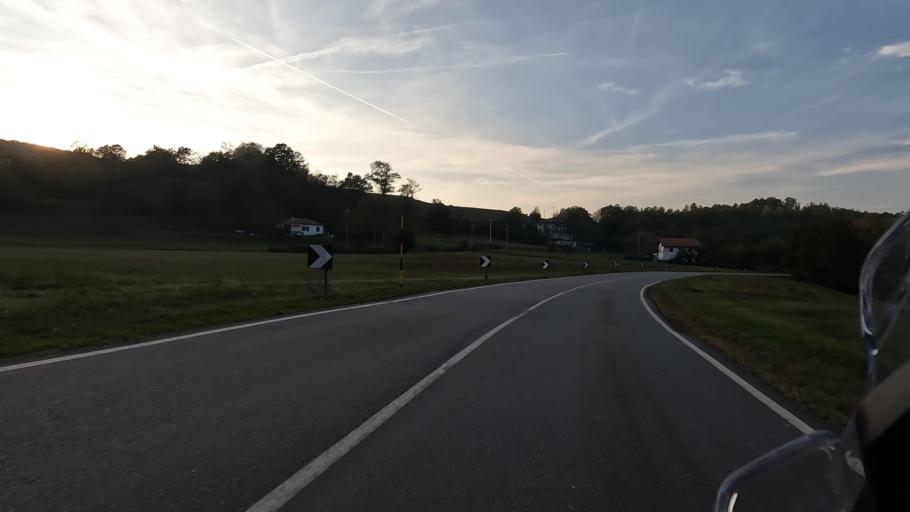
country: IT
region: Liguria
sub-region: Provincia di Savona
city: Sassello
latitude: 44.5105
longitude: 8.4752
